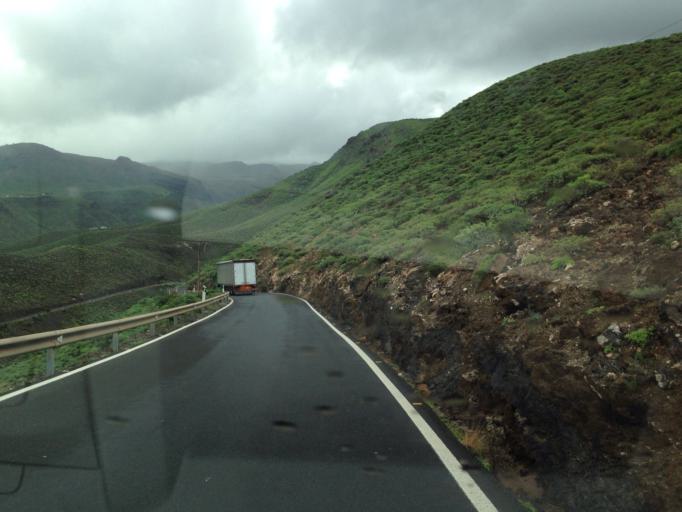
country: ES
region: Canary Islands
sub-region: Provincia de Las Palmas
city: Agaete
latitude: 28.0936
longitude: -15.7052
